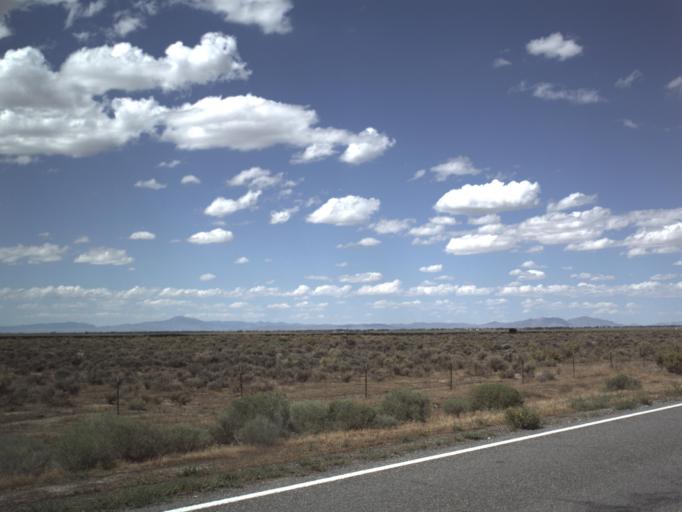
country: US
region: Utah
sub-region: Millard County
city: Delta
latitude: 39.2642
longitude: -112.4496
